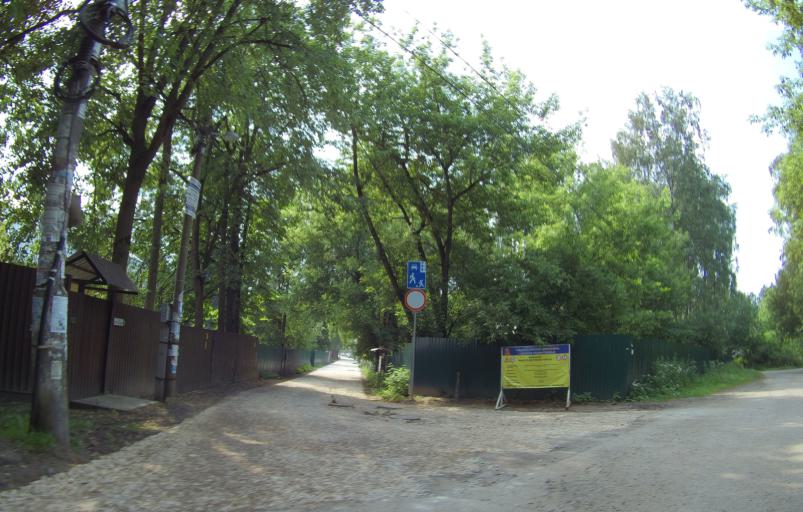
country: RU
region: Moskovskaya
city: Udel'naya
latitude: 55.6335
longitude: 38.0114
